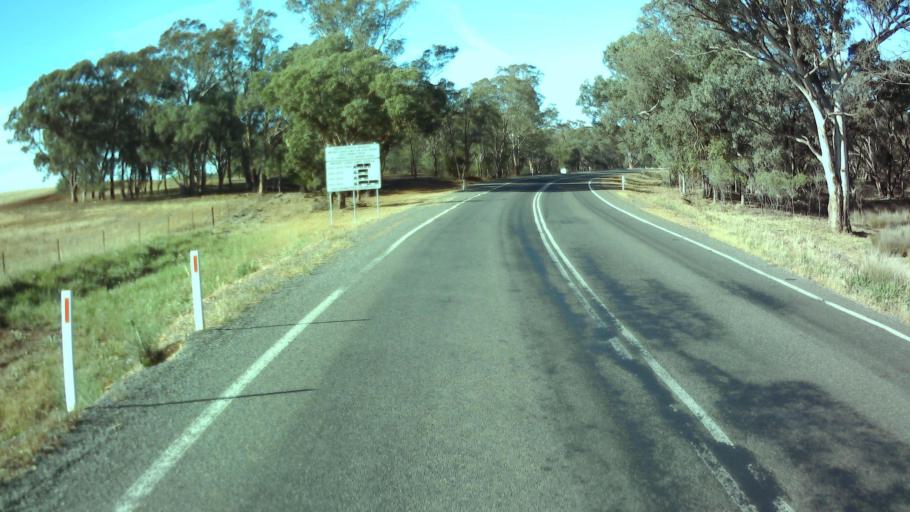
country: AU
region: New South Wales
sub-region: Weddin
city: Grenfell
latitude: -33.9992
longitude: 148.1318
